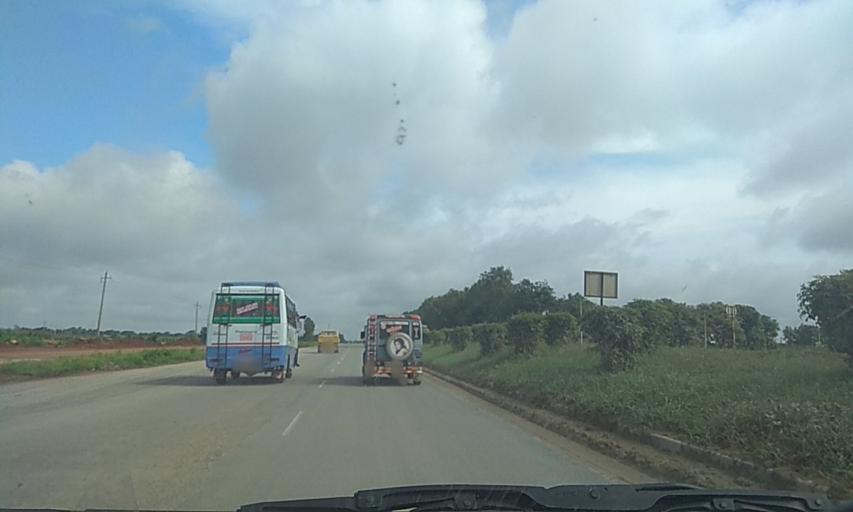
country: IN
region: Karnataka
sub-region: Haveri
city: Shiggaon
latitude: 15.0446
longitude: 75.1707
